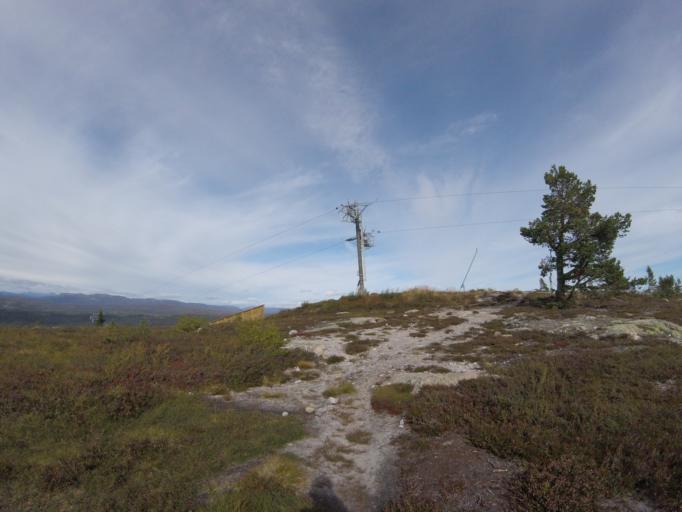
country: NO
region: Buskerud
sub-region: Flesberg
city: Lampeland
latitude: 59.7484
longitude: 9.4175
